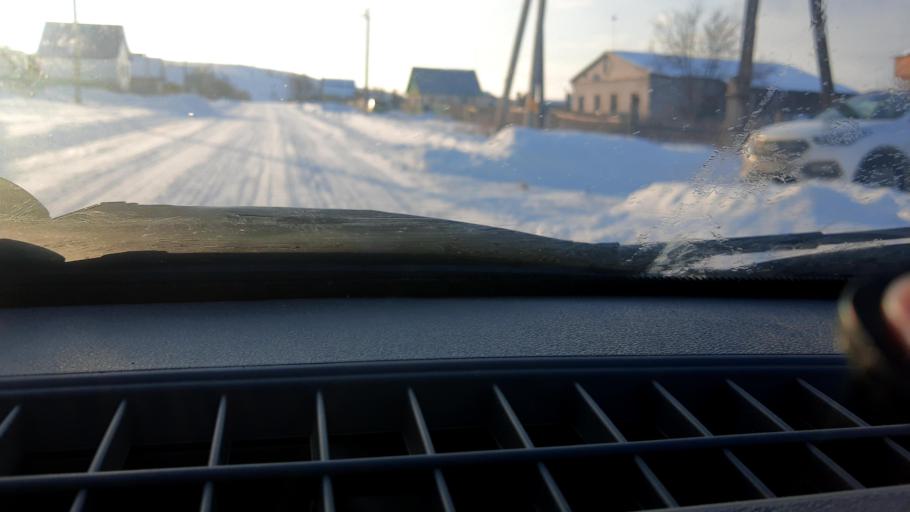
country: RU
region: Bashkortostan
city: Kushnarenkovo
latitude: 55.1362
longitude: 55.6183
